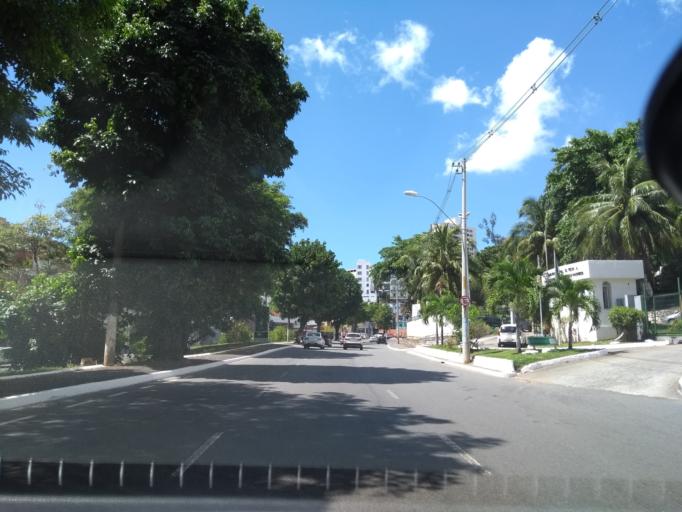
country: BR
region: Bahia
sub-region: Salvador
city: Salvador
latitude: -12.9922
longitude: -38.5126
